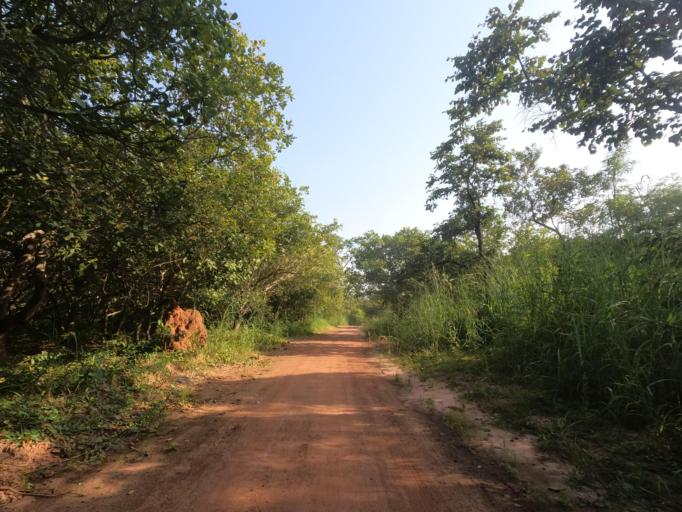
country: SN
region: Sedhiou
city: Sedhiou
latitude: 12.4163
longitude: -15.7321
